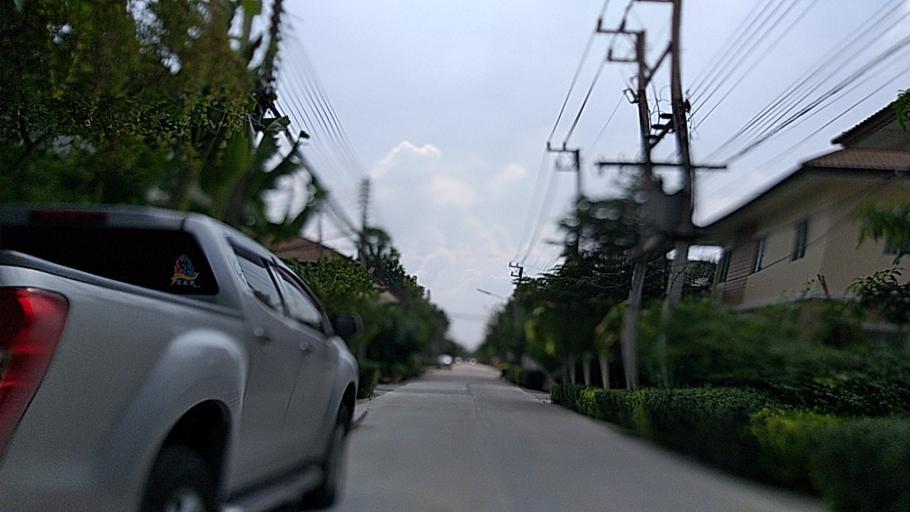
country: TH
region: Pathum Thani
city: Ban Rangsit
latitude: 14.0459
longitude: 100.7652
